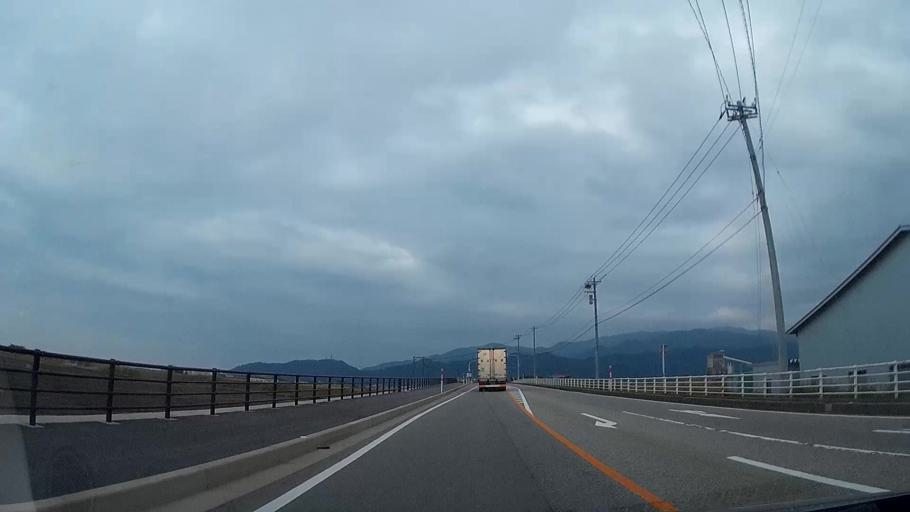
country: JP
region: Toyama
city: Nyuzen
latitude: 36.9460
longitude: 137.5384
